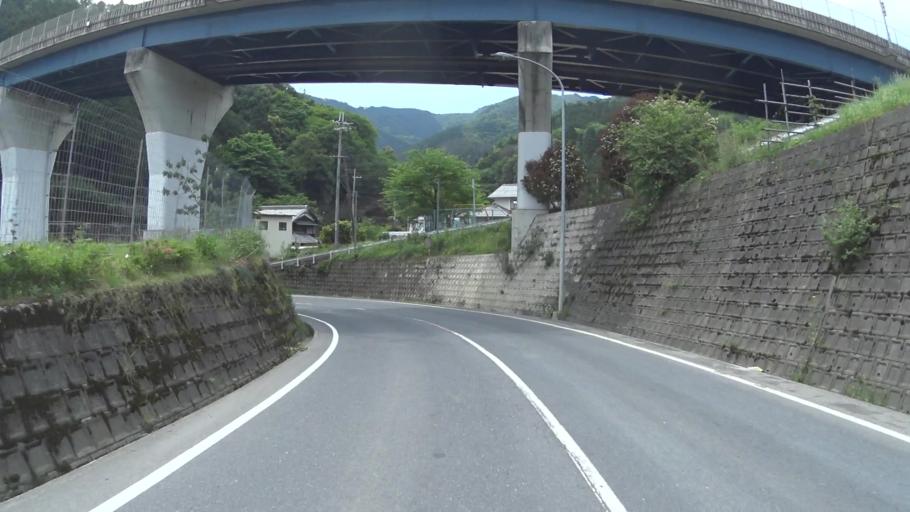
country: JP
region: Shiga Prefecture
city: Kitahama
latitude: 35.1666
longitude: 135.8604
